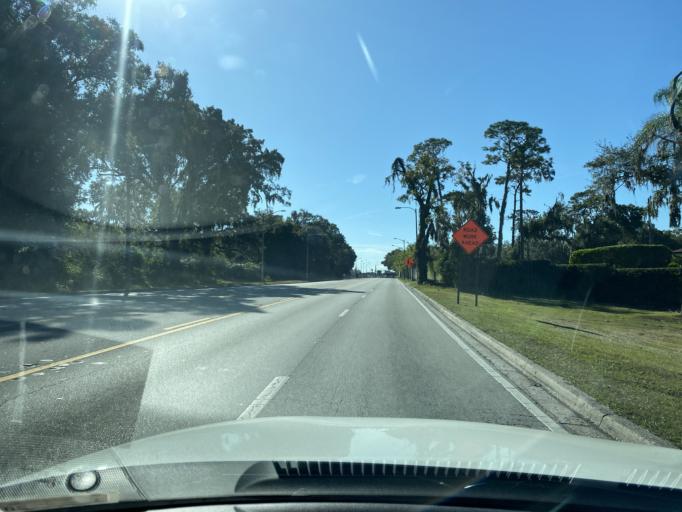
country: US
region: Florida
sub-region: Orange County
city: Orlando
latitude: 28.5565
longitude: -81.3957
